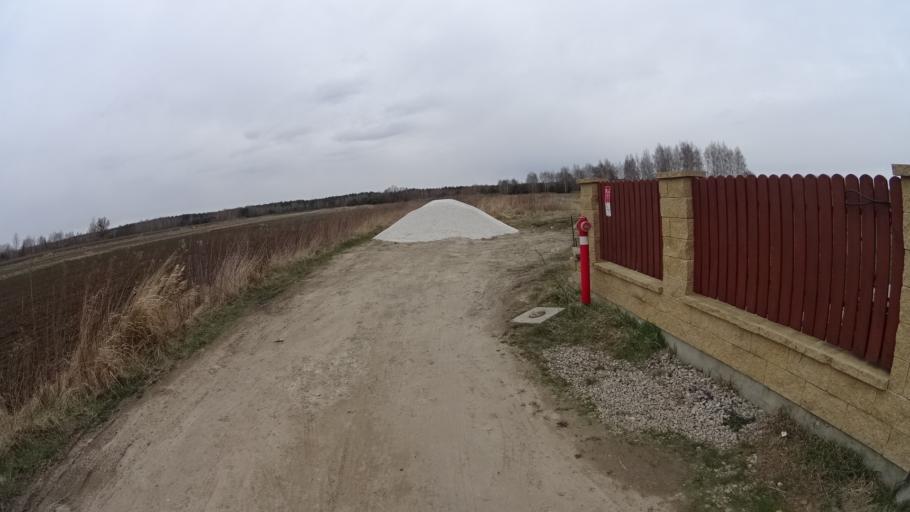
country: PL
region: Masovian Voivodeship
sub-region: Powiat warszawski zachodni
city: Hornowek
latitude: 52.2687
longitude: 20.7895
